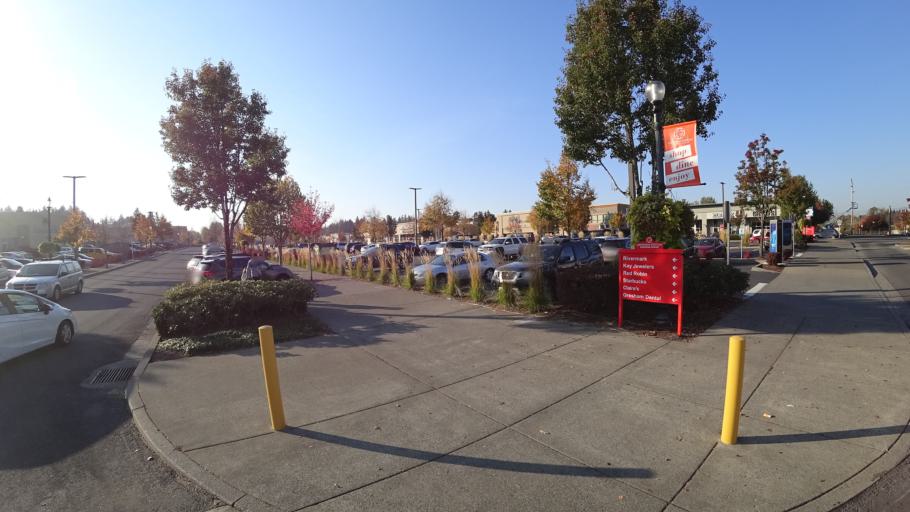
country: US
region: Oregon
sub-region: Multnomah County
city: Gresham
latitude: 45.5053
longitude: -122.4381
